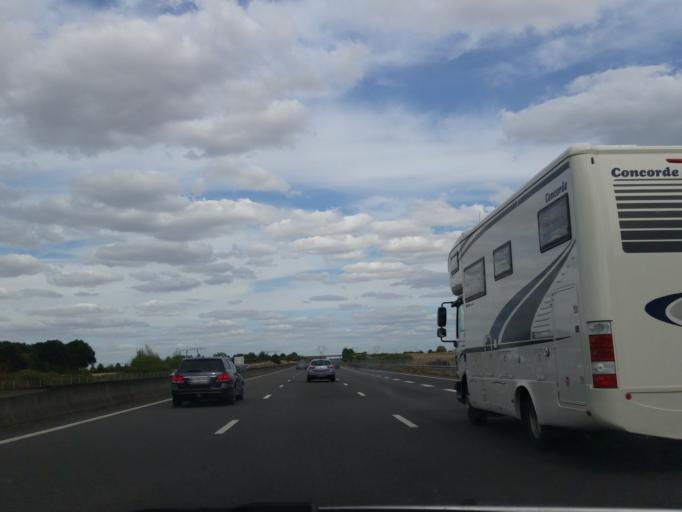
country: FR
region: Centre
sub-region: Departement du Loir-et-Cher
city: Herbault
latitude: 47.6071
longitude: 1.1247
